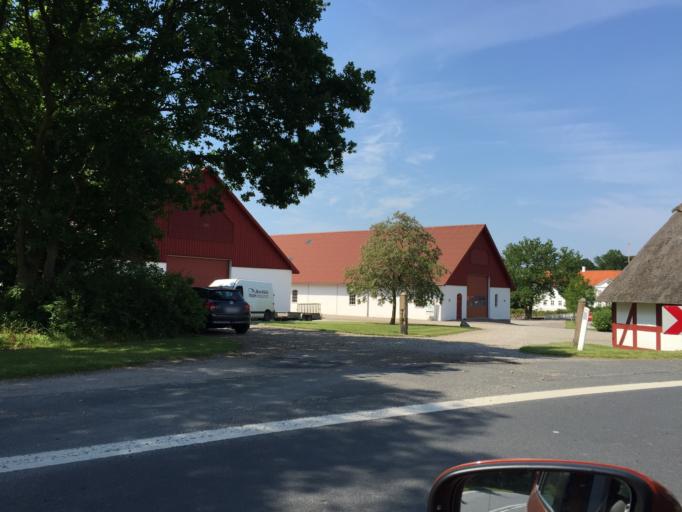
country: DK
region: South Denmark
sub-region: Kerteminde Kommune
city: Kerteminde
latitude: 55.5339
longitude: 10.6481
